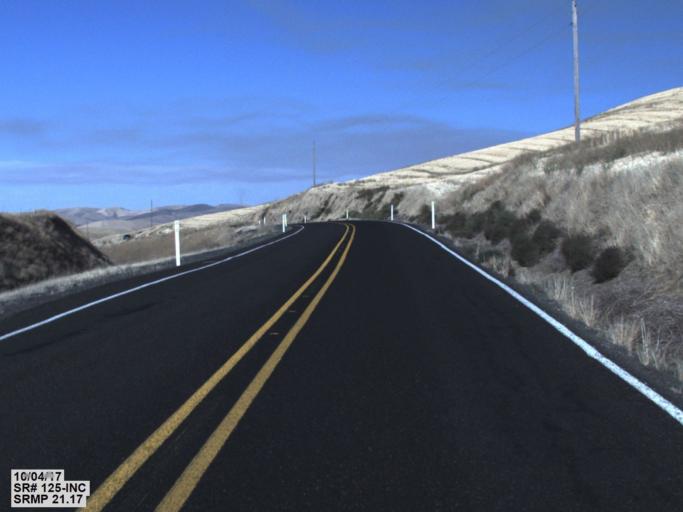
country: US
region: Washington
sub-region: Walla Walla County
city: Waitsburg
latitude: 46.2644
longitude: -118.3521
